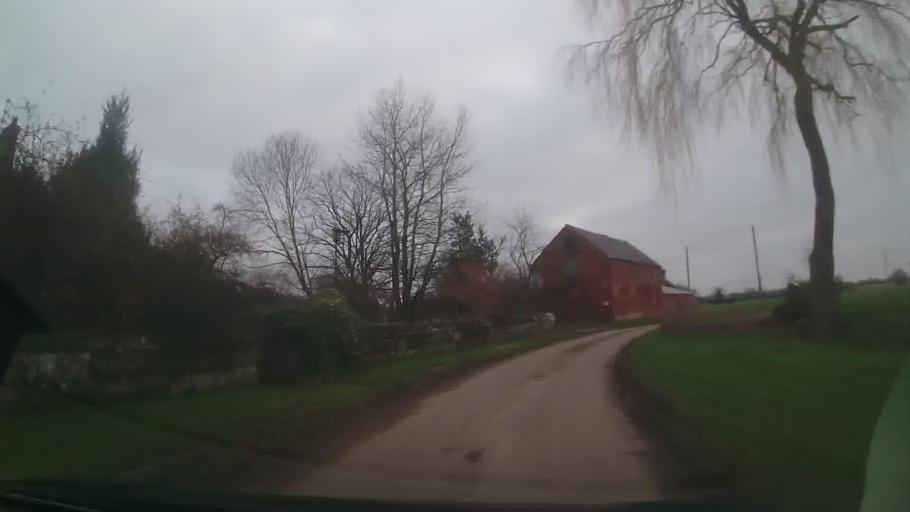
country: GB
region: England
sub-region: Shropshire
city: Petton
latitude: 52.8006
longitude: -2.8296
